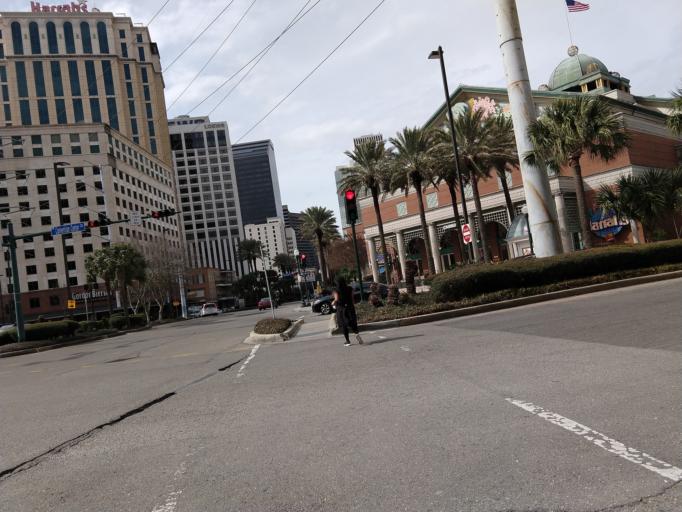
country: US
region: Louisiana
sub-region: Orleans Parish
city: New Orleans
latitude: 29.9483
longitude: -90.0639
